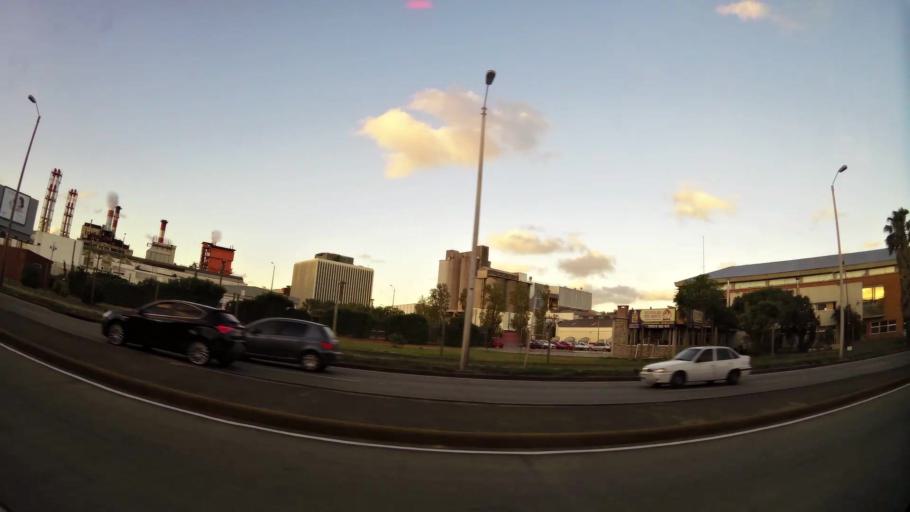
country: UY
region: Montevideo
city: Montevideo
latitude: -34.8889
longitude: -56.1967
